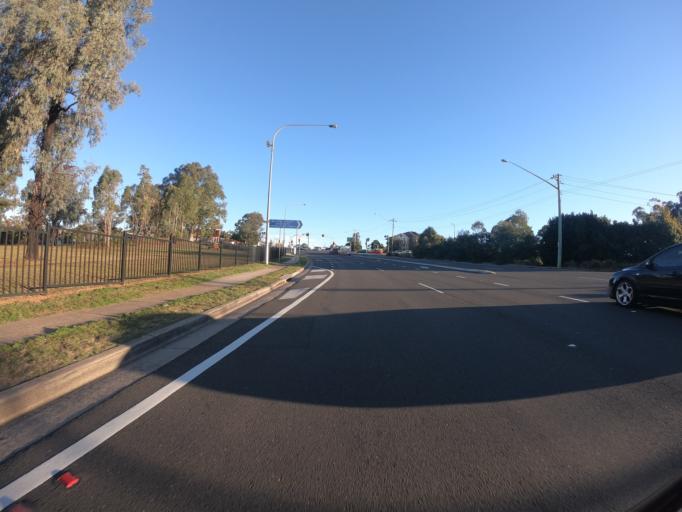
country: AU
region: New South Wales
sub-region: Campbelltown Municipality
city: Campbelltown
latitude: -34.0741
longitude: 150.8089
